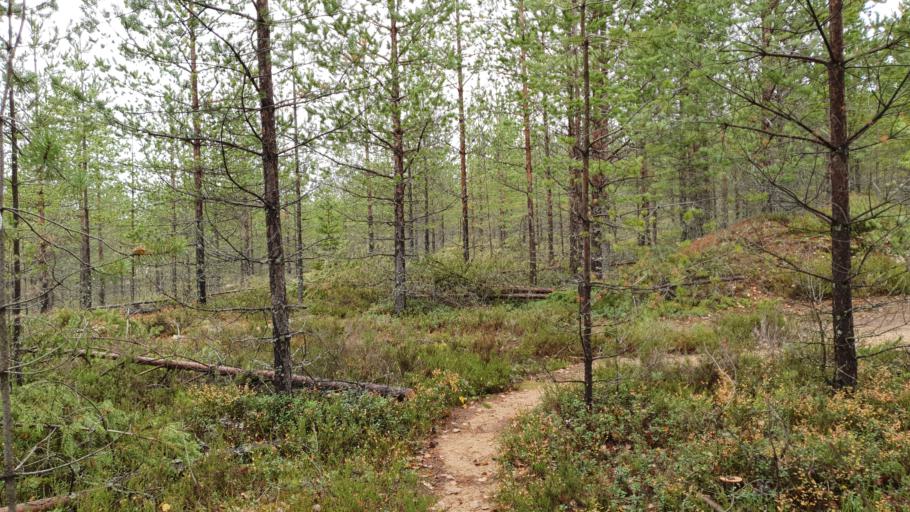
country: FI
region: Kainuu
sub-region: Kehys-Kainuu
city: Kuhmo
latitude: 64.1497
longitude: 29.4003
